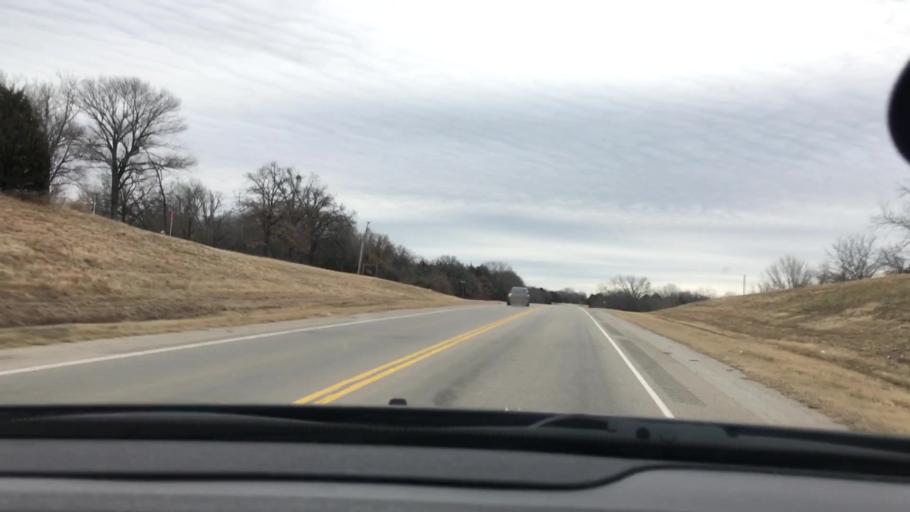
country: US
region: Oklahoma
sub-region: Johnston County
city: Tishomingo
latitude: 34.2374
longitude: -96.7760
